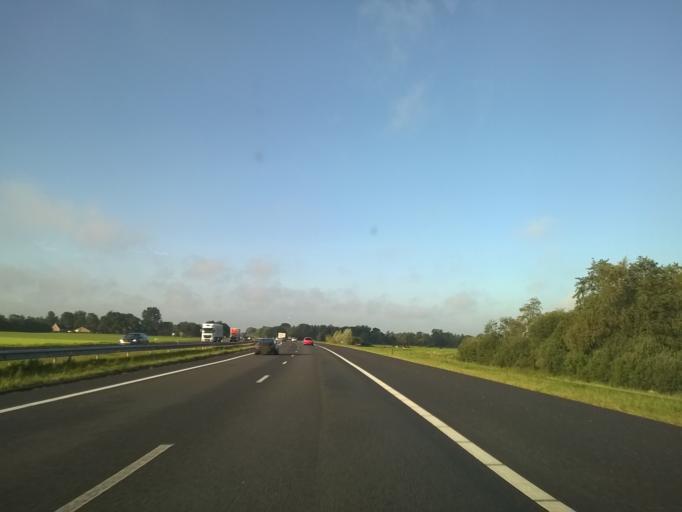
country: NL
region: Groningen
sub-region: Gemeente Leek
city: Leek
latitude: 53.1914
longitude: 6.3953
